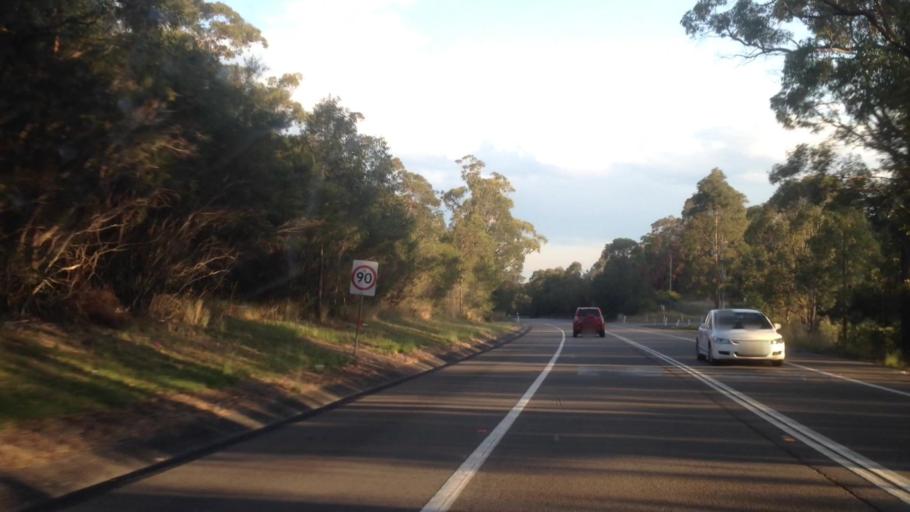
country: AU
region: New South Wales
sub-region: Lake Macquarie Shire
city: Dora Creek
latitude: -33.0061
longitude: 151.4892
